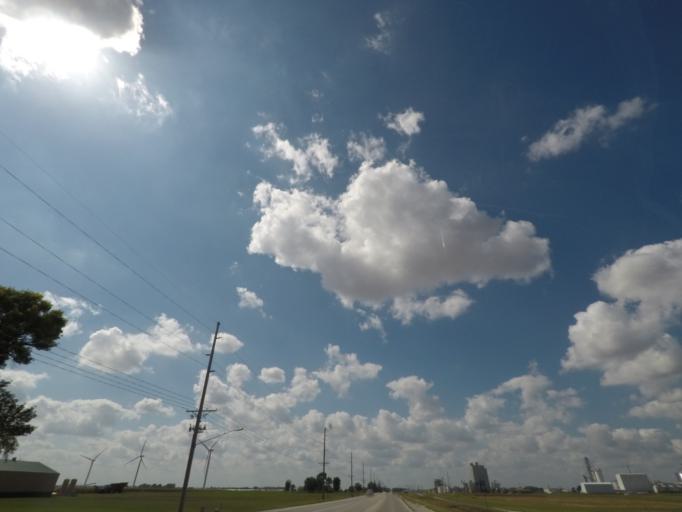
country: US
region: Iowa
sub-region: Story County
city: Nevada
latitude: 42.0231
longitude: -93.5024
